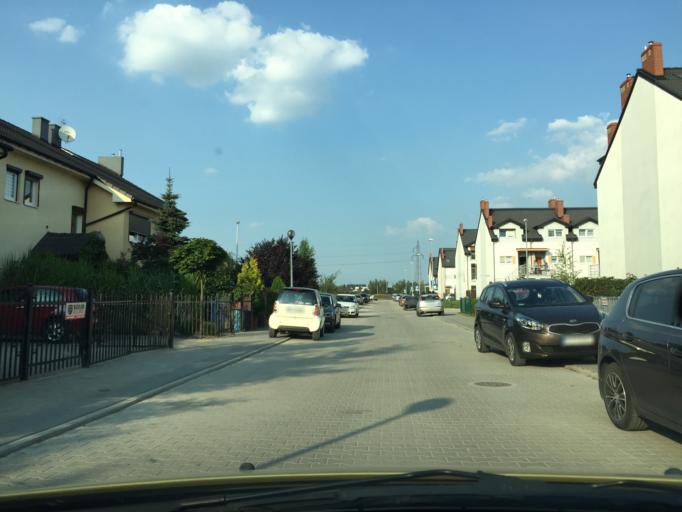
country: PL
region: Greater Poland Voivodeship
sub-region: Powiat poznanski
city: Plewiska
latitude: 52.3753
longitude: 16.8158
